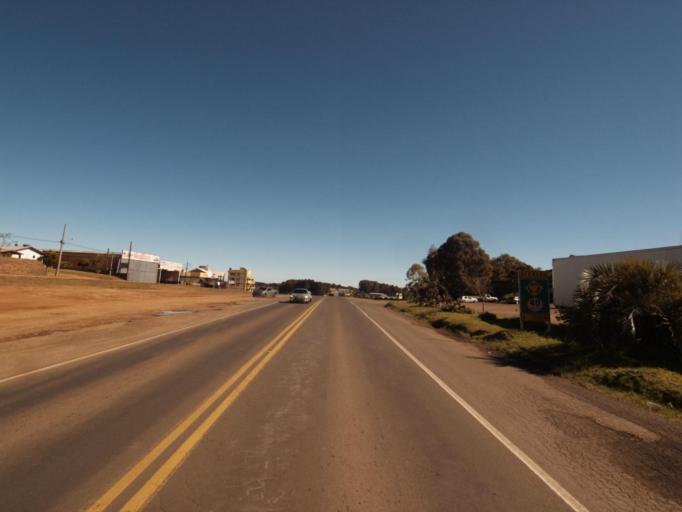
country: BR
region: Santa Catarina
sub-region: Xanxere
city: Xanxere
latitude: -26.8563
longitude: -52.2588
